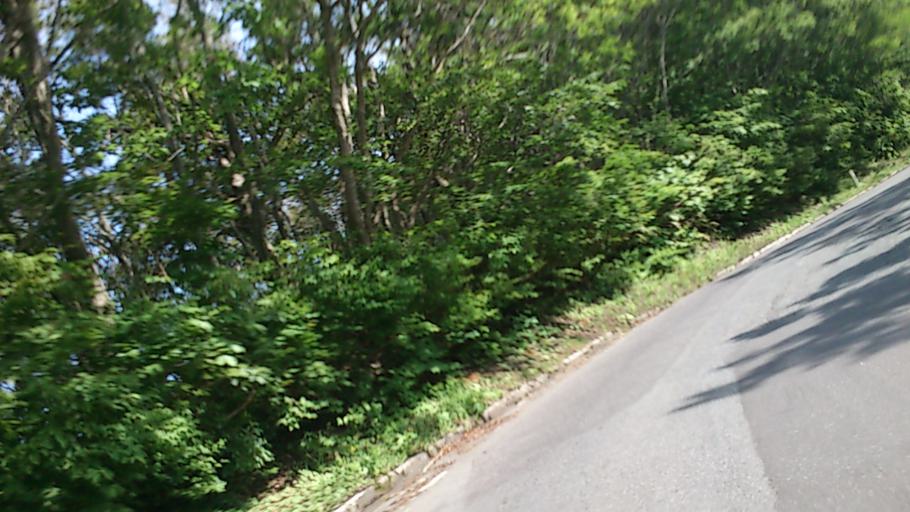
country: JP
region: Aomori
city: Aomori Shi
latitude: 40.7205
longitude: 140.8084
